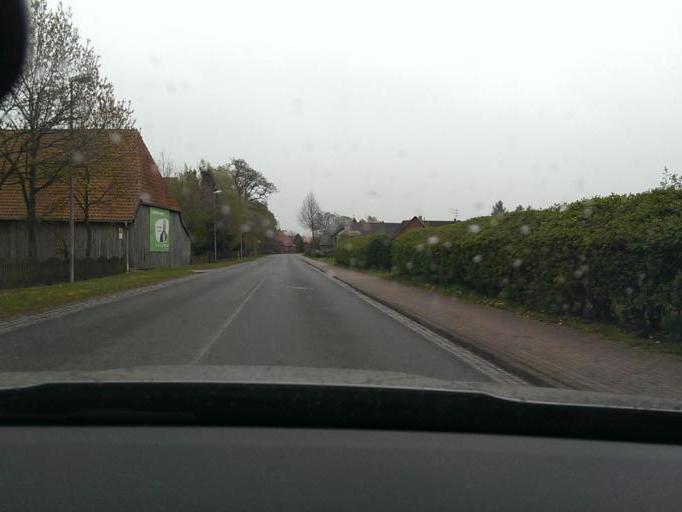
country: DE
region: Lower Saxony
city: Steimbke
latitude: 52.6517
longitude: 9.4879
